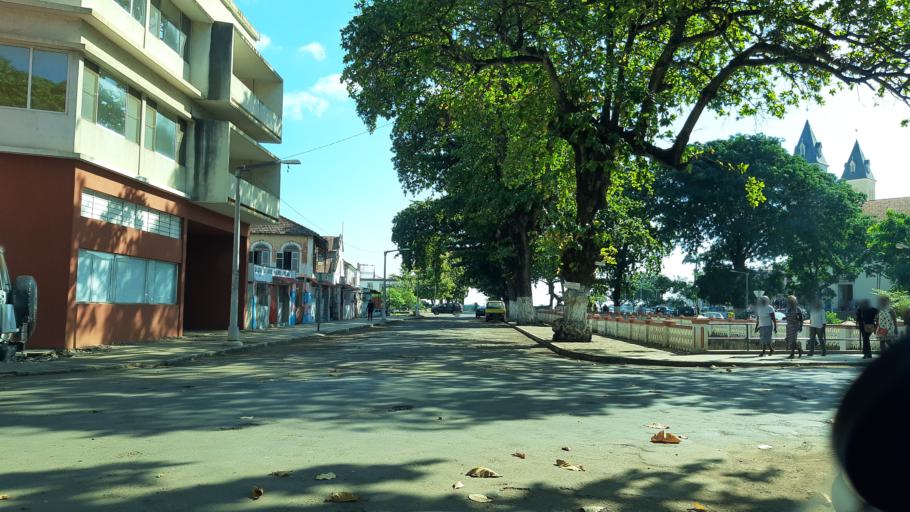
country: ST
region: Sao Tome Island
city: Sao Tome
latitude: 0.3377
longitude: 6.7318
